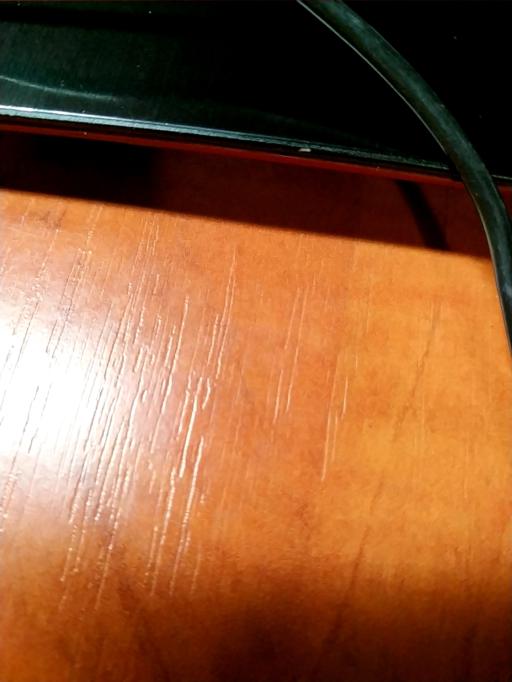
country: RU
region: Tverskaya
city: Zubtsov
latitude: 56.2294
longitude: 34.5308
